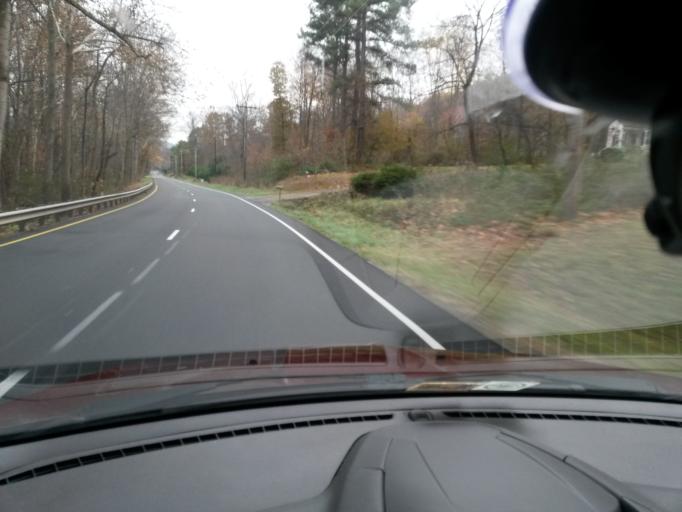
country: US
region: Virginia
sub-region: Albemarle County
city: Crozet
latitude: 37.9411
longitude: -78.6685
